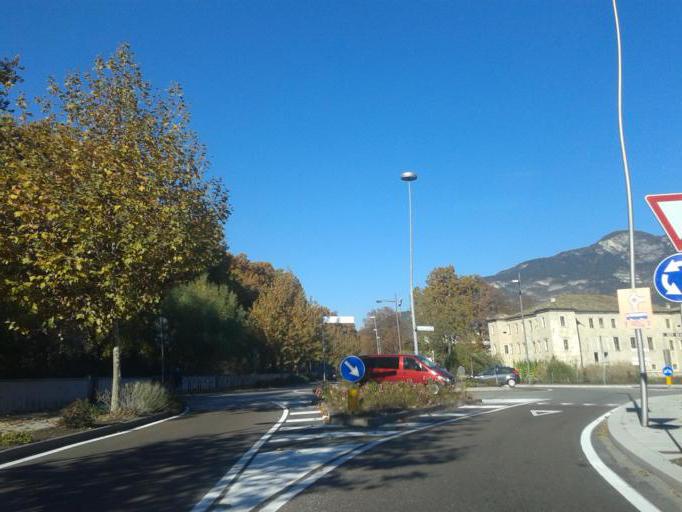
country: IT
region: Trentino-Alto Adige
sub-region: Provincia di Trento
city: Trento
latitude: 46.0619
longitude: 11.1128
